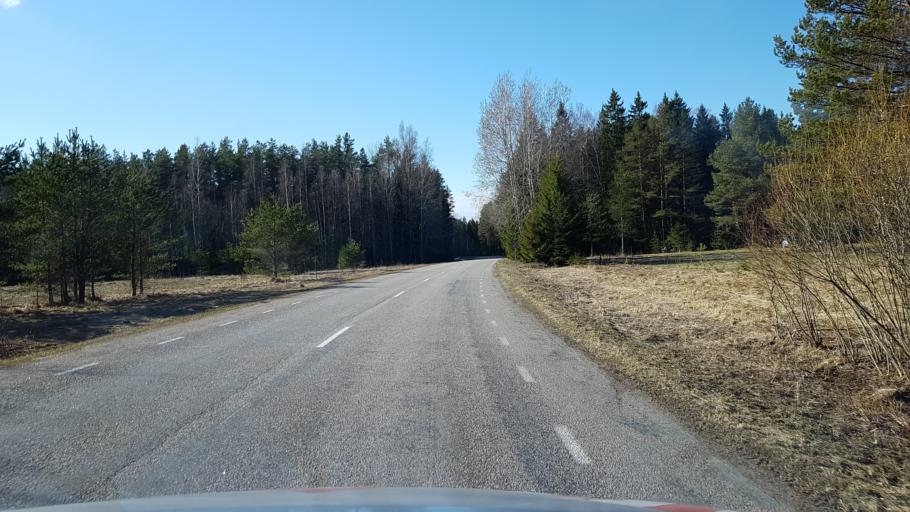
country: EE
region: Laeaene-Virumaa
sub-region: Kadrina vald
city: Kadrina
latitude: 59.5434
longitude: 26.0271
